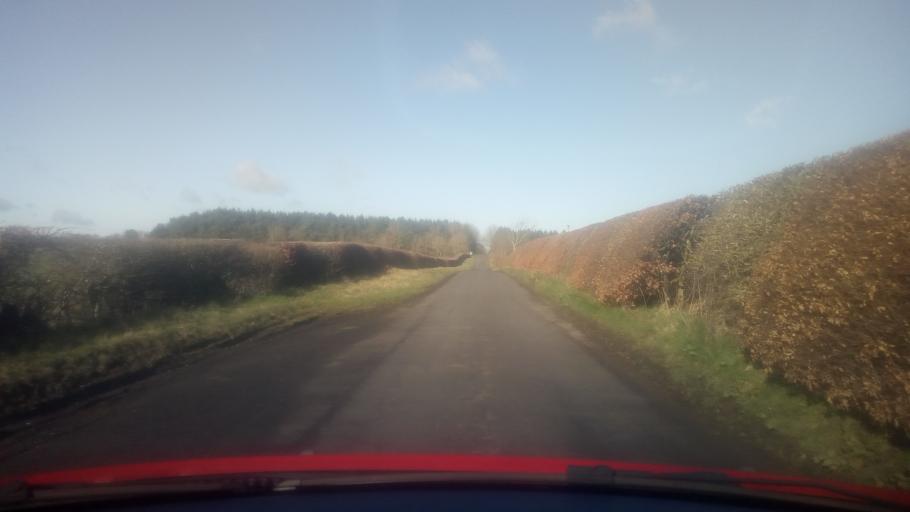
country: GB
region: Scotland
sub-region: The Scottish Borders
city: Saint Boswells
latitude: 55.5346
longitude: -2.6496
